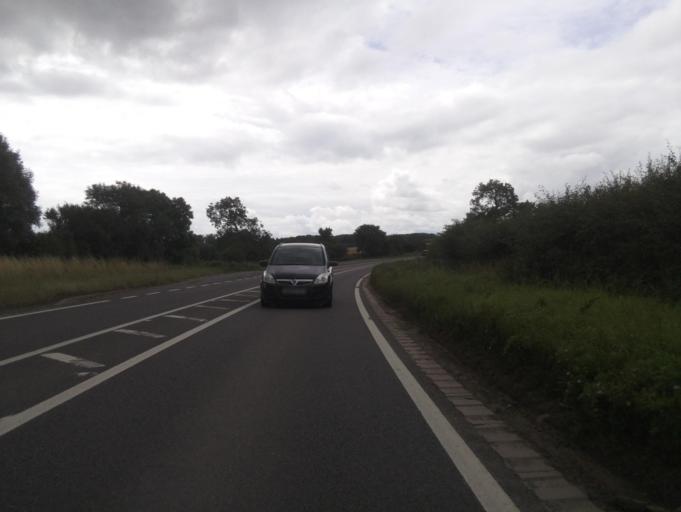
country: GB
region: England
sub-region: District of Rutland
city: Ketton
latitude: 52.5879
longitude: -0.5535
